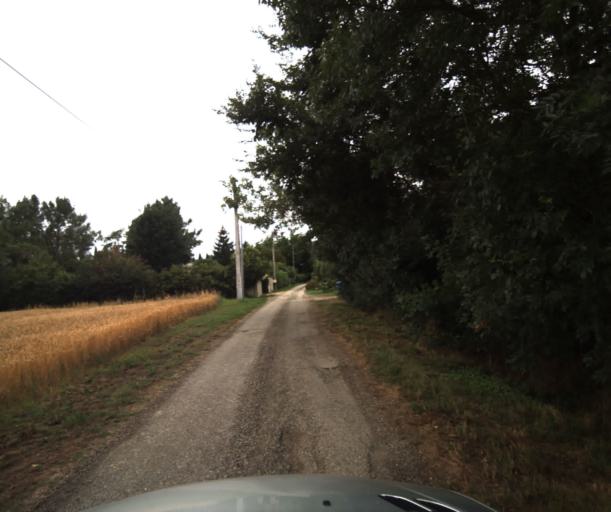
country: FR
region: Midi-Pyrenees
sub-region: Departement de la Haute-Garonne
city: Labarthe-sur-Leze
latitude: 43.4652
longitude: 1.4177
